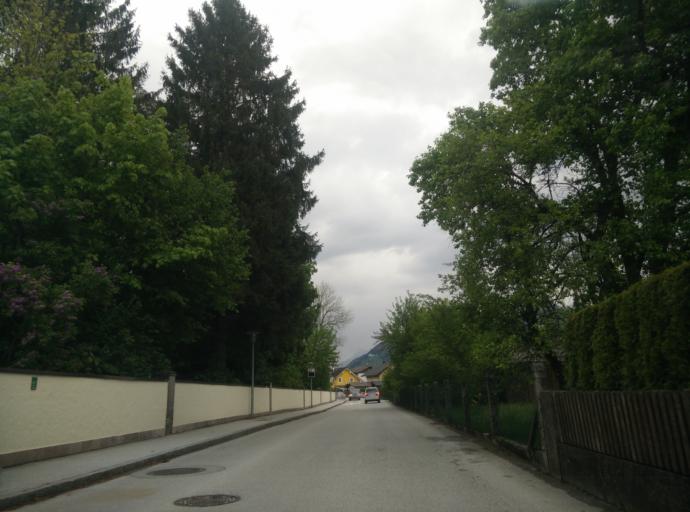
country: AT
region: Salzburg
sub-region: Politischer Bezirk Hallein
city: Oberalm
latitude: 47.7031
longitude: 13.0892
